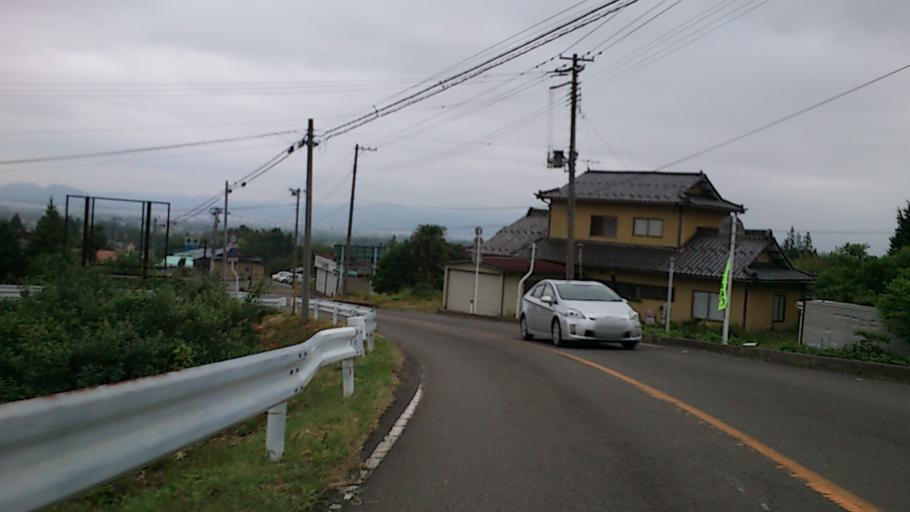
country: JP
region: Fukushima
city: Fukushima-shi
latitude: 37.7548
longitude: 140.3566
